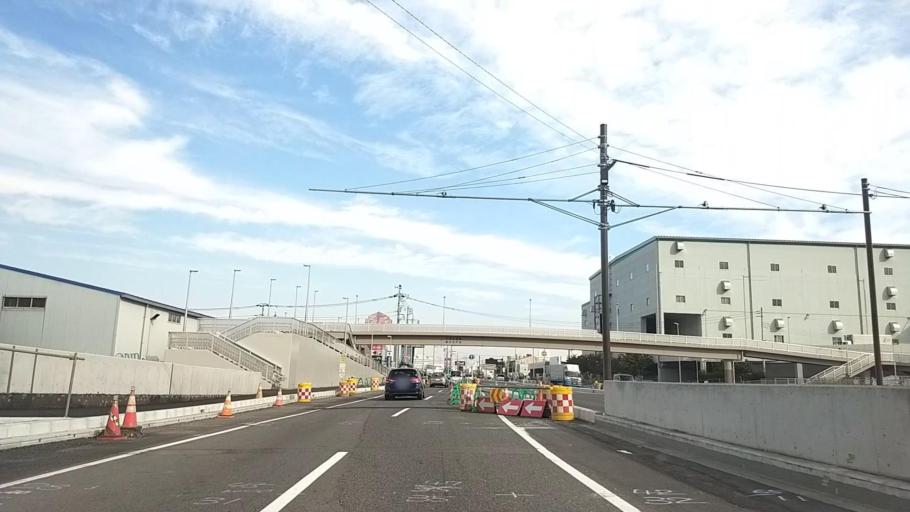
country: JP
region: Kanagawa
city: Atsugi
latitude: 35.4071
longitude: 139.3615
